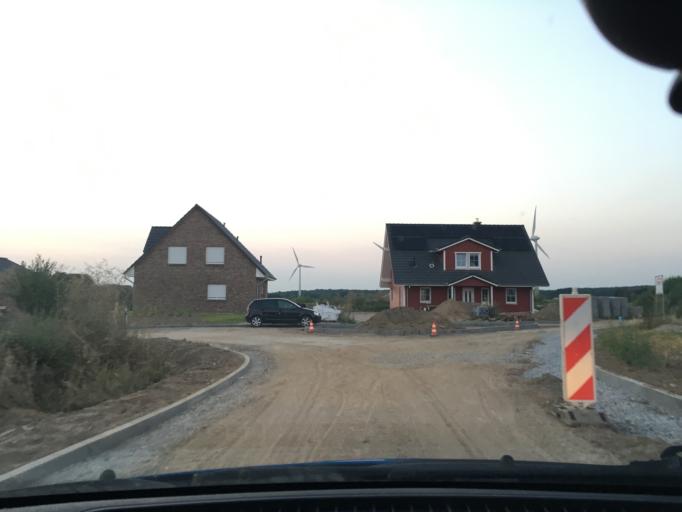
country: DE
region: Lower Saxony
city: Embsen
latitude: 53.1814
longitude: 10.3507
